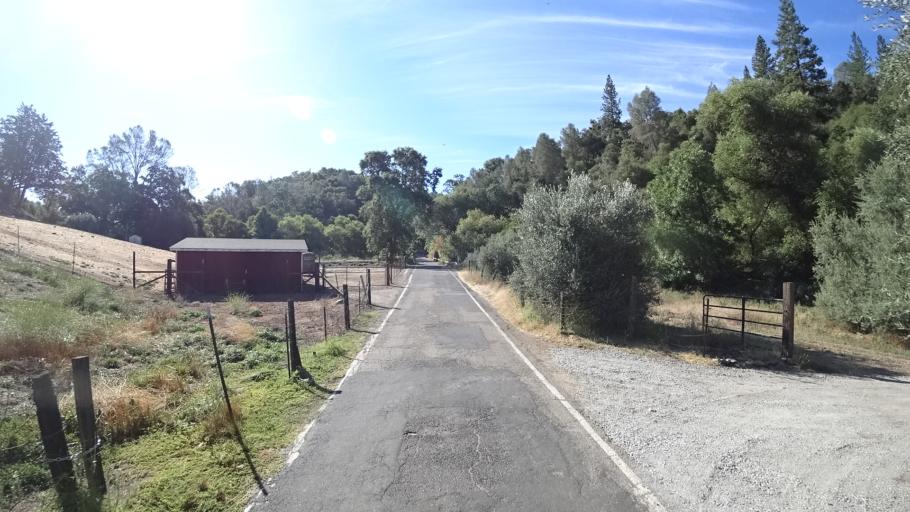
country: US
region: California
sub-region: Calaveras County
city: San Andreas
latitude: 38.1568
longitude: -120.6107
